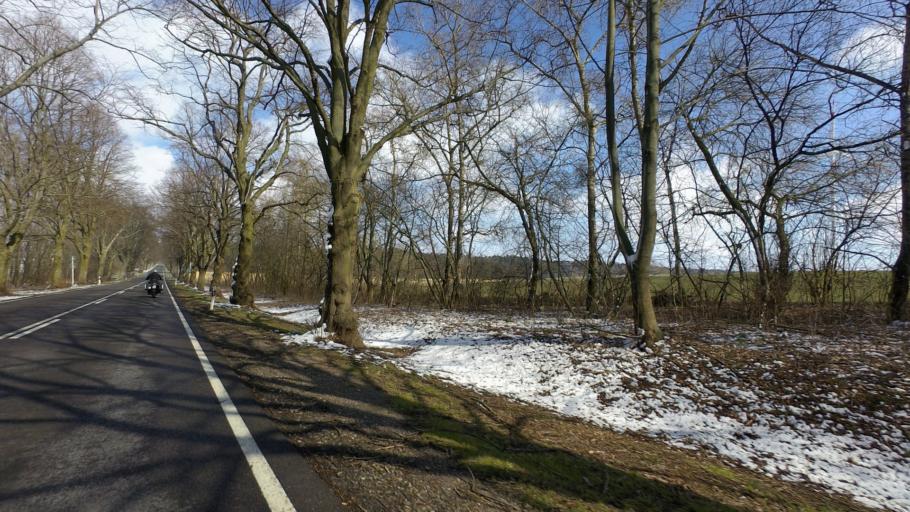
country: DE
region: Brandenburg
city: Werftpfuhl
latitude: 52.7045
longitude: 13.8368
